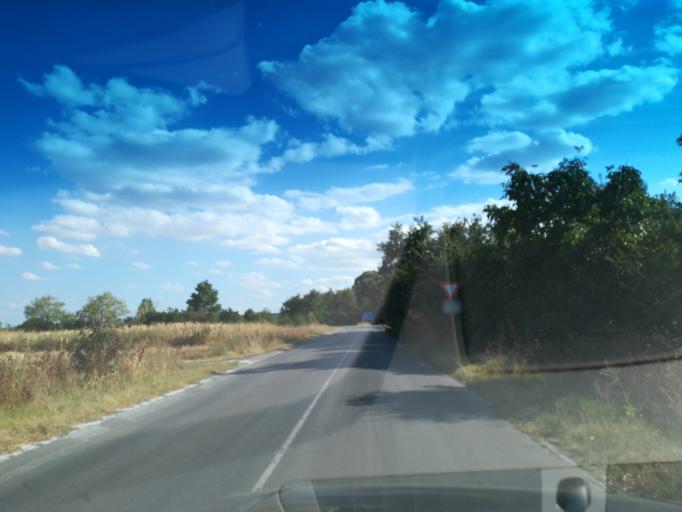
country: BG
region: Khaskovo
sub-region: Obshtina Mineralni Bani
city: Mineralni Bani
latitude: 42.0179
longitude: 25.4299
